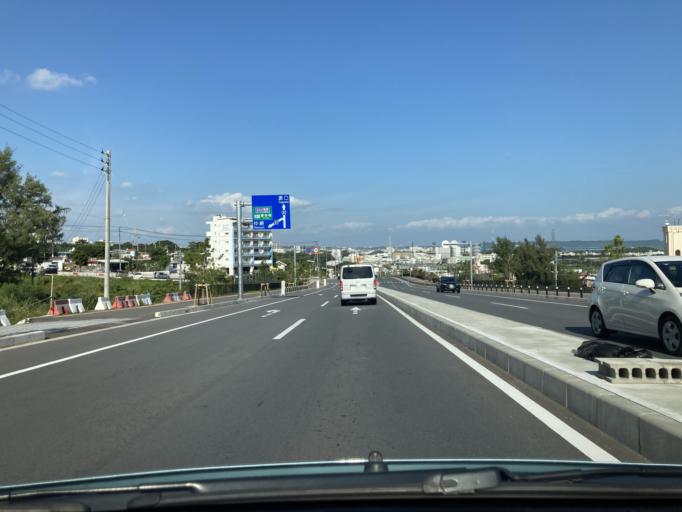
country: JP
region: Okinawa
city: Chatan
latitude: 26.3003
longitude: 127.8039
